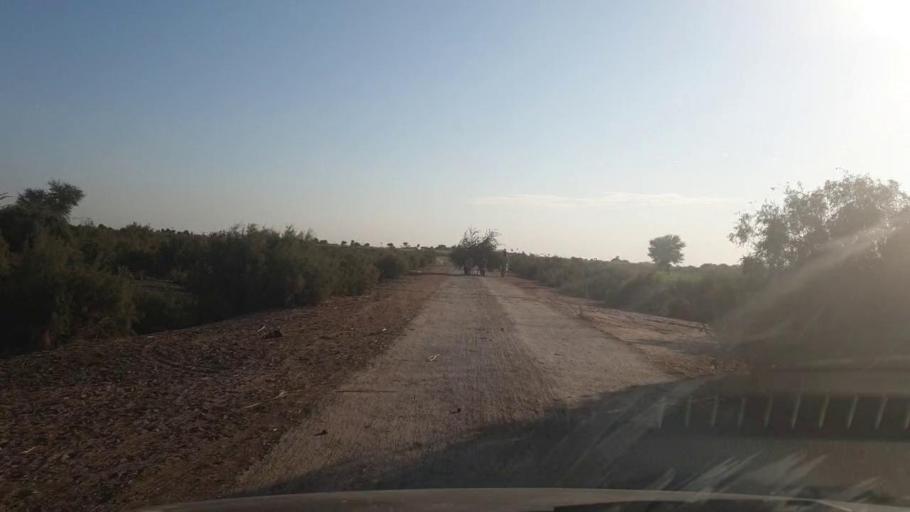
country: PK
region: Sindh
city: Sinjhoro
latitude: 26.0515
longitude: 68.8711
